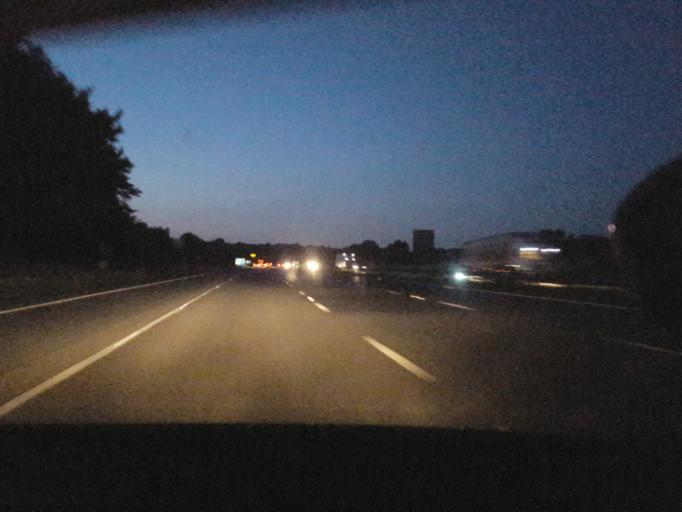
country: GB
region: England
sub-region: Leicestershire
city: Markfield
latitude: 52.7040
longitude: -1.2922
